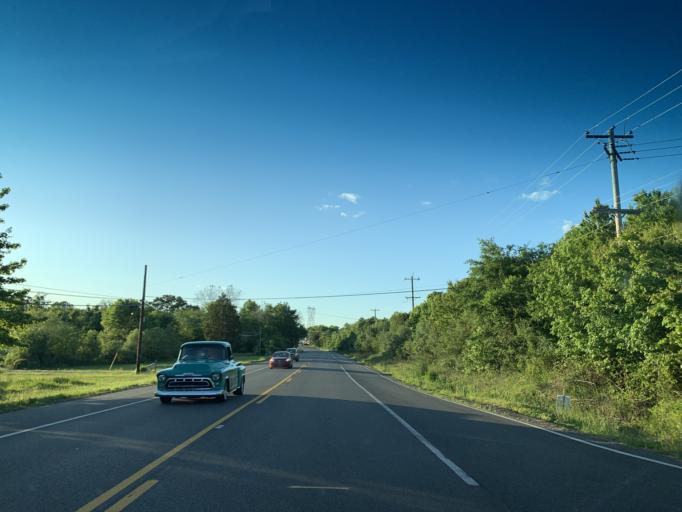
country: US
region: Maryland
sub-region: Cecil County
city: Elkton
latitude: 39.6393
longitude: -75.8439
